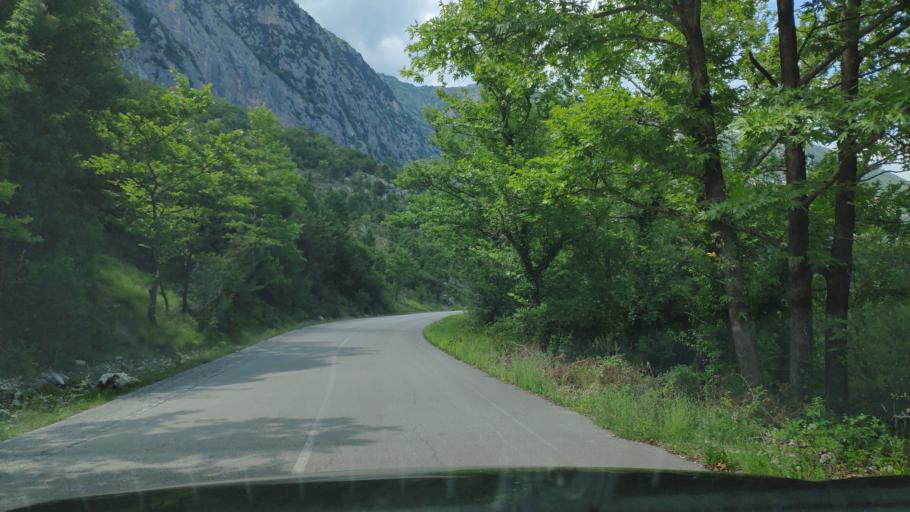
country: GR
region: Epirus
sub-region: Nomos Artas
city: Agios Dimitrios
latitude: 39.4287
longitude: 21.0166
